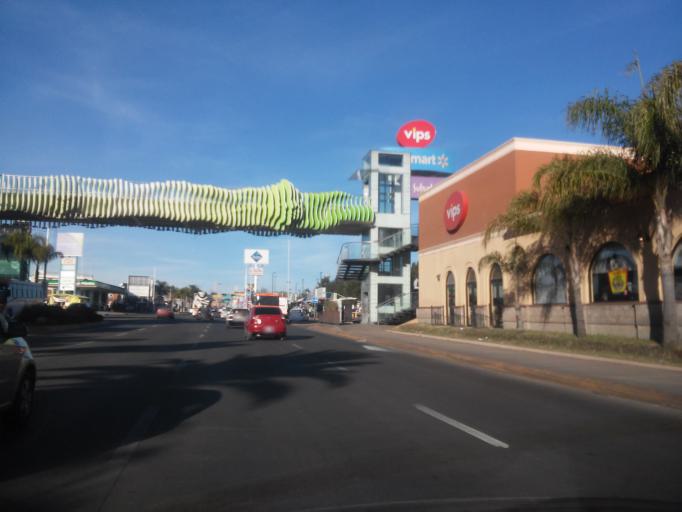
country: MX
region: Durango
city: Victoria de Durango
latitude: 24.0348
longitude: -104.6525
